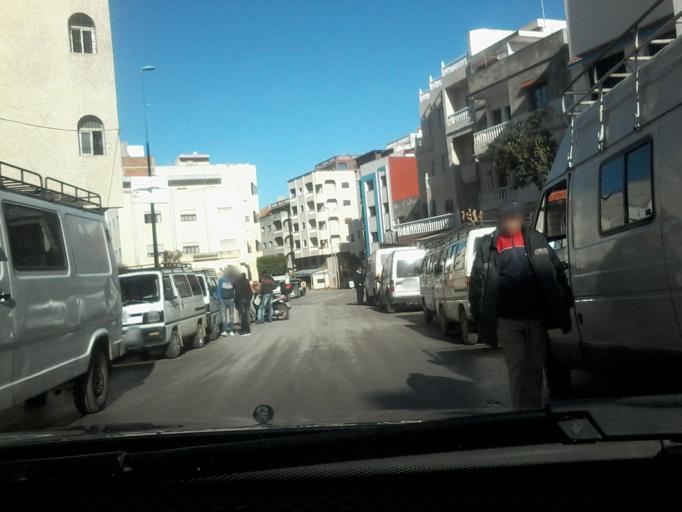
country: MA
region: Tanger-Tetouan
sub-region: Tetouan
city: Martil
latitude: 35.6837
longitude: -5.3263
